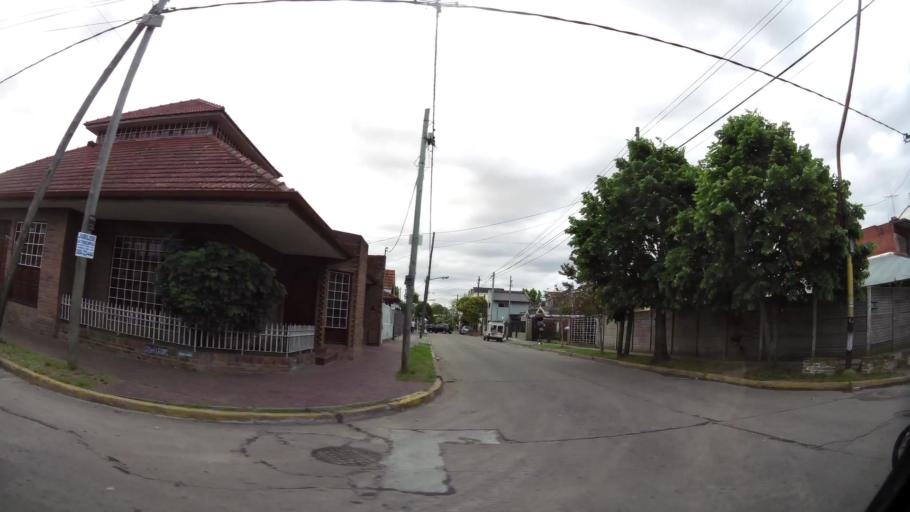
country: AR
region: Buenos Aires
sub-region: Partido de Quilmes
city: Quilmes
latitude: -34.7466
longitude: -58.2311
